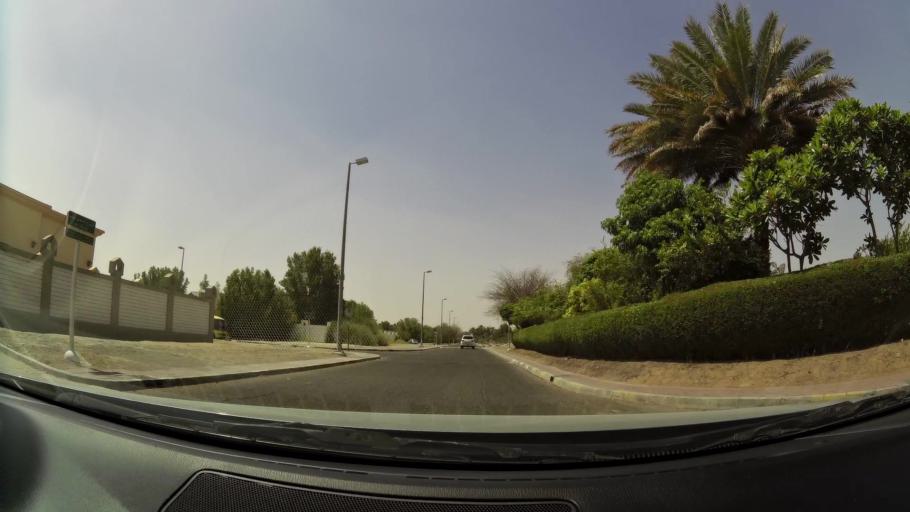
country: AE
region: Abu Dhabi
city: Al Ain
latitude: 24.2357
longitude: 55.7125
